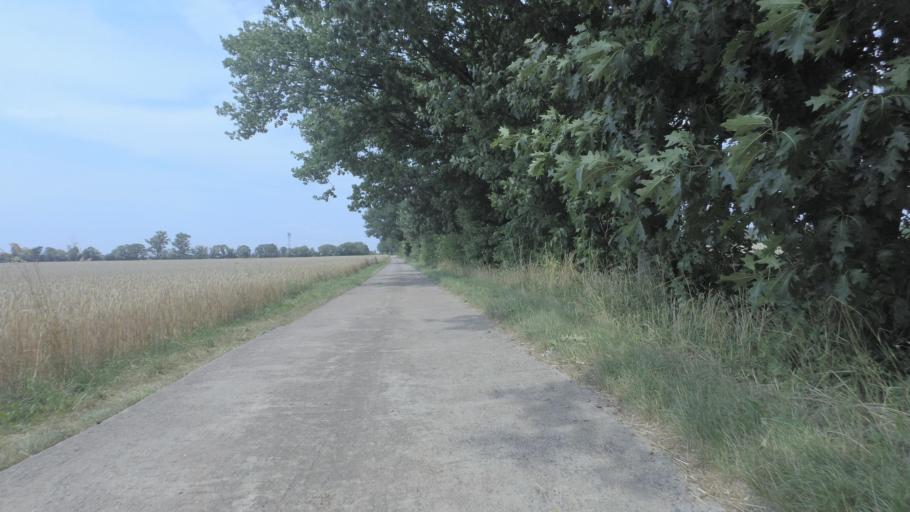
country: DE
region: Brandenburg
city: Rangsdorf
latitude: 52.3338
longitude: 13.4602
